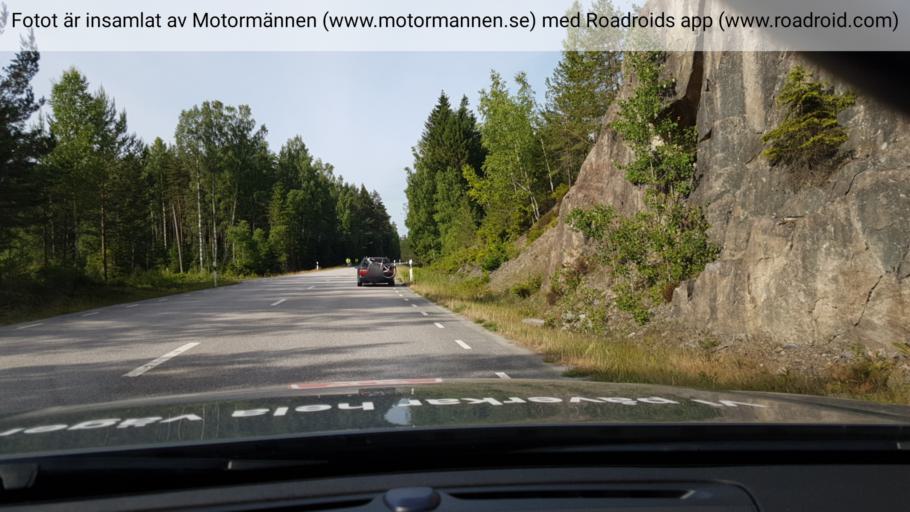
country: SE
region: Vaestra Goetaland
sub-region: Karlsborgs Kommun
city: Karlsborg
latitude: 58.6451
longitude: 14.5656
